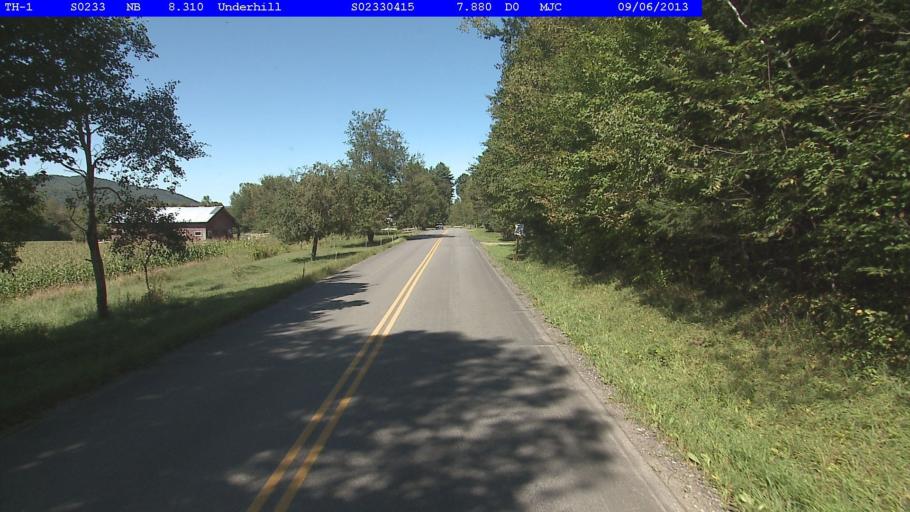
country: US
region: Vermont
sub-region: Chittenden County
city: Jericho
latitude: 44.5782
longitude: -72.8628
